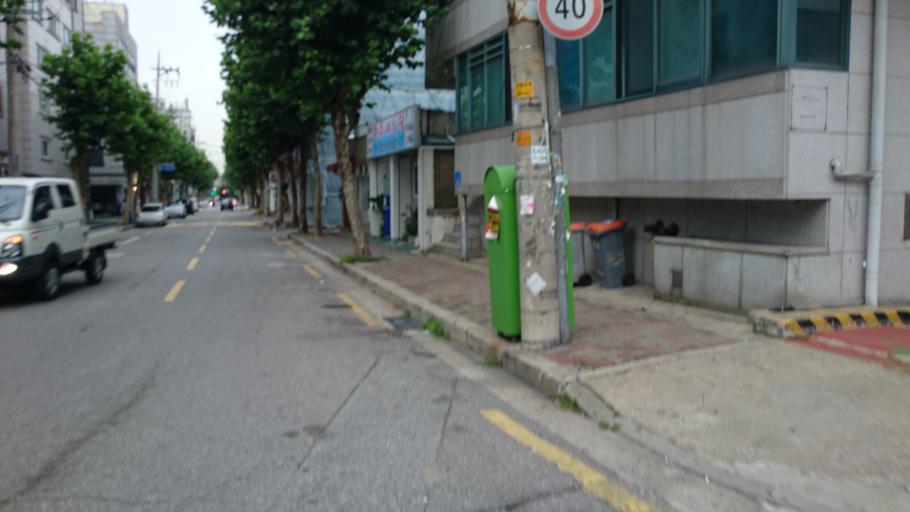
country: KR
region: Seoul
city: Seoul
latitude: 37.5648
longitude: 126.9242
